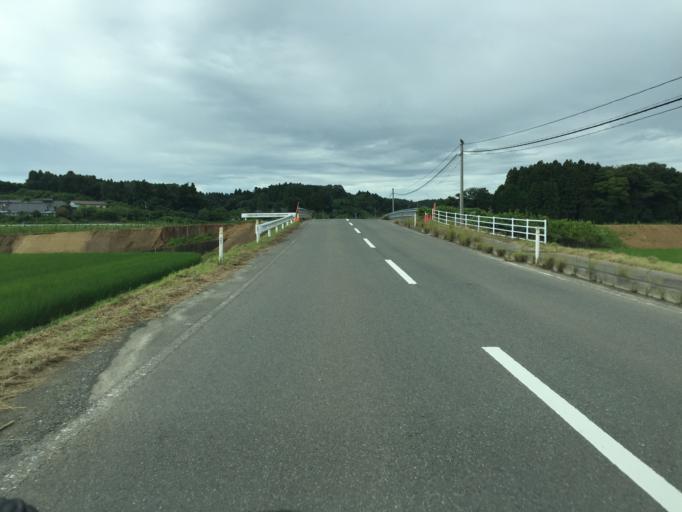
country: JP
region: Miyagi
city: Marumori
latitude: 37.7844
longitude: 140.9557
